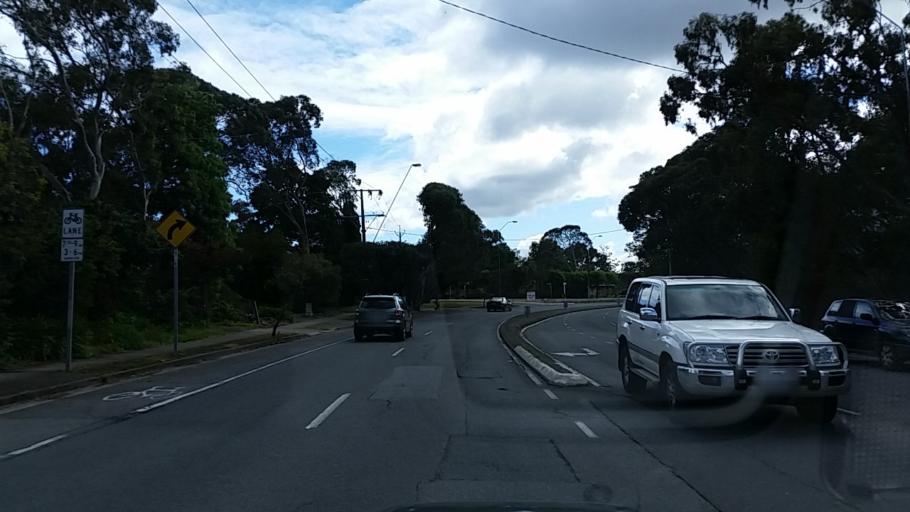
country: AU
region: South Australia
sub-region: Mitcham
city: Blackwood
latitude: -35.0221
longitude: 138.6083
